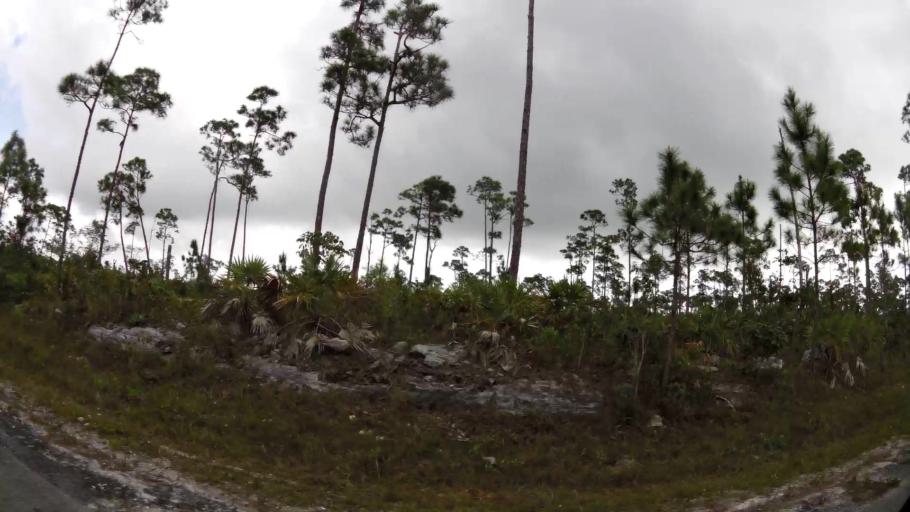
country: BS
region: Freeport
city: Lucaya
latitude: 26.5578
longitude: -78.5783
